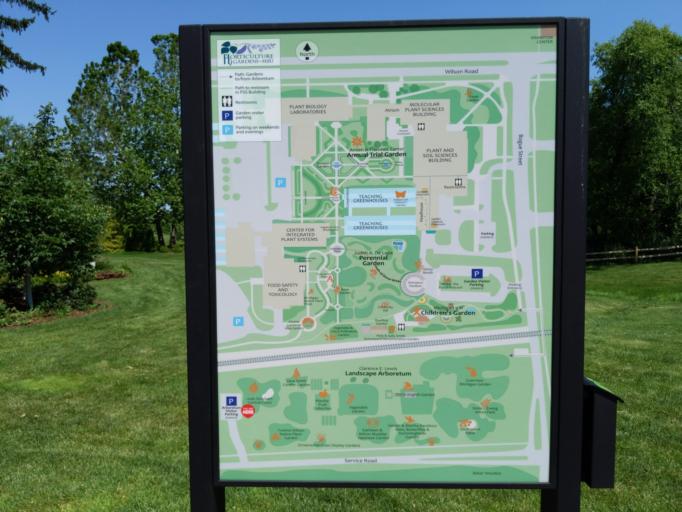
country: US
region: Michigan
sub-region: Ingham County
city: East Lansing
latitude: 42.7196
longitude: -84.4754
